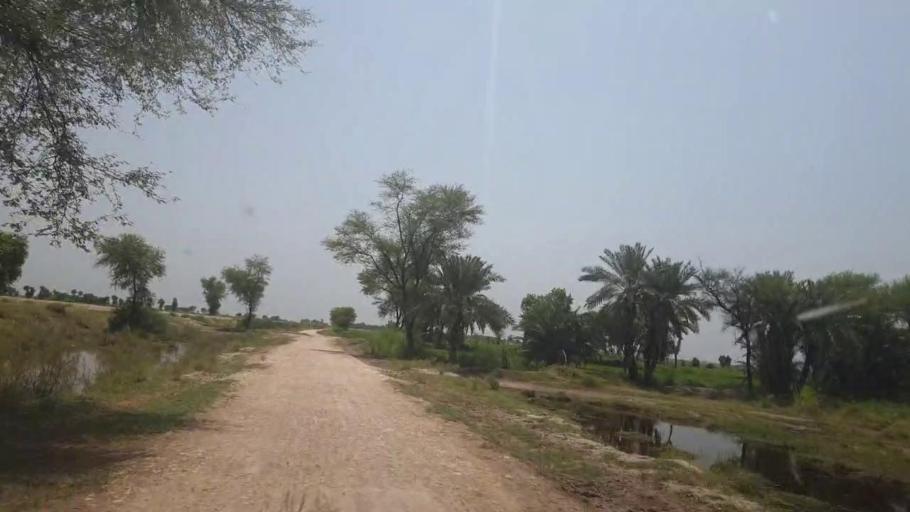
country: PK
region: Sindh
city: Lakhi
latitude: 27.8587
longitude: 68.6645
